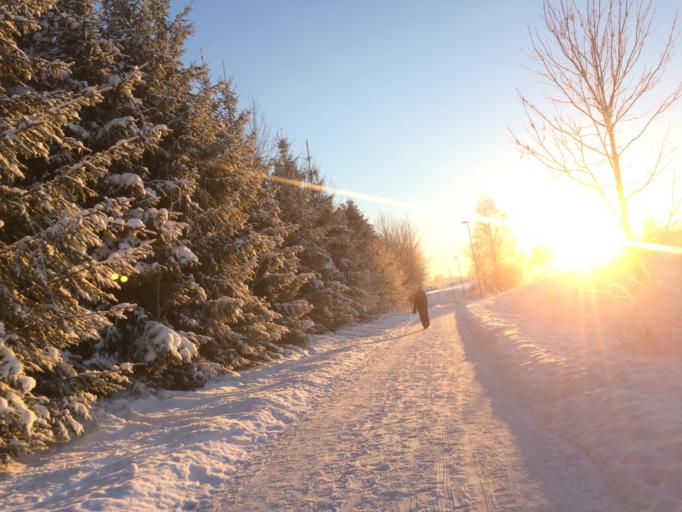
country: NO
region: Akershus
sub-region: Ski
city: Ski
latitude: 59.7050
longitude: 10.8340
